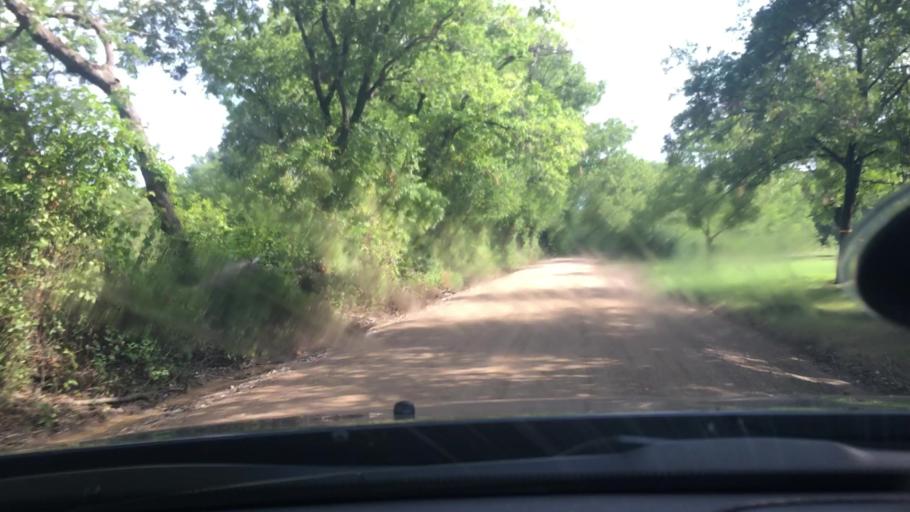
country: US
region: Oklahoma
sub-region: Atoka County
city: Atoka
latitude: 34.4537
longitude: -96.0659
